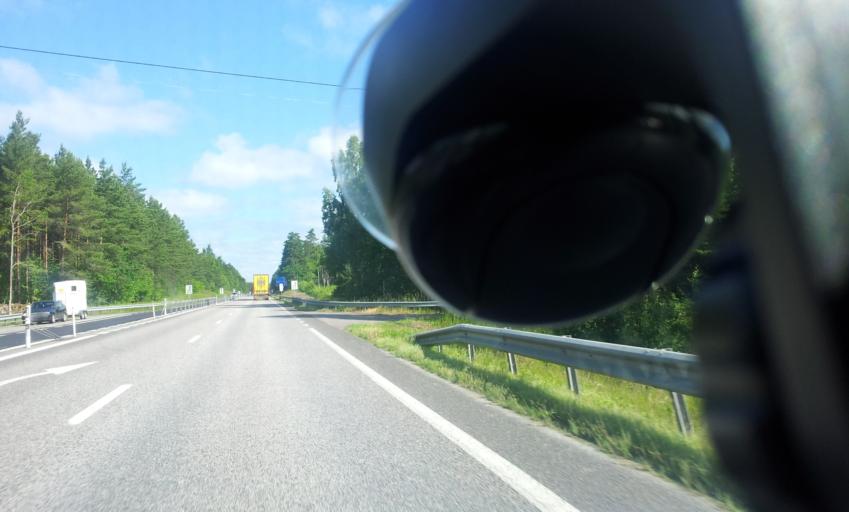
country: SE
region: Kalmar
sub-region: Kalmar Kommun
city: Lindsdal
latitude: 56.8241
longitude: 16.3684
